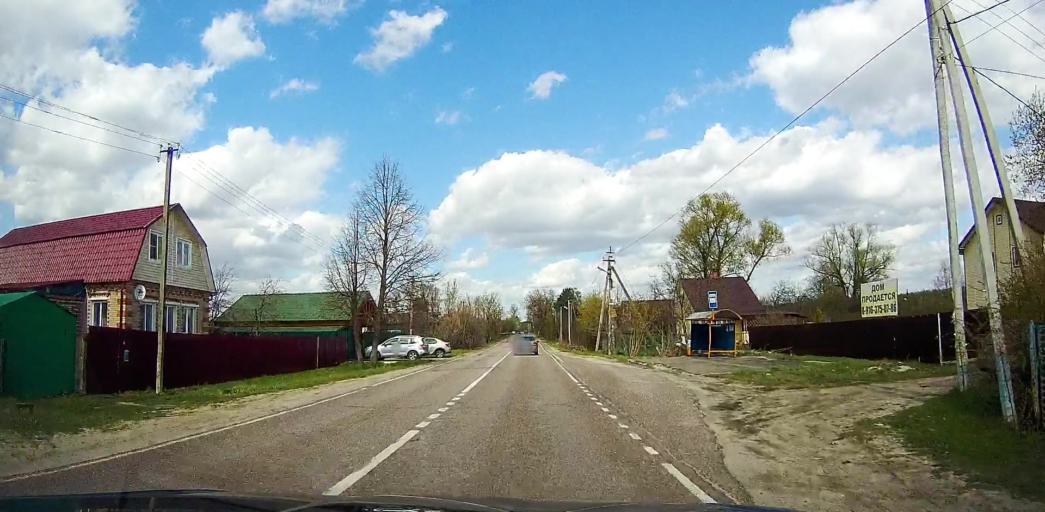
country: RU
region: Moskovskaya
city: Davydovo
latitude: 55.5806
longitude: 38.8246
